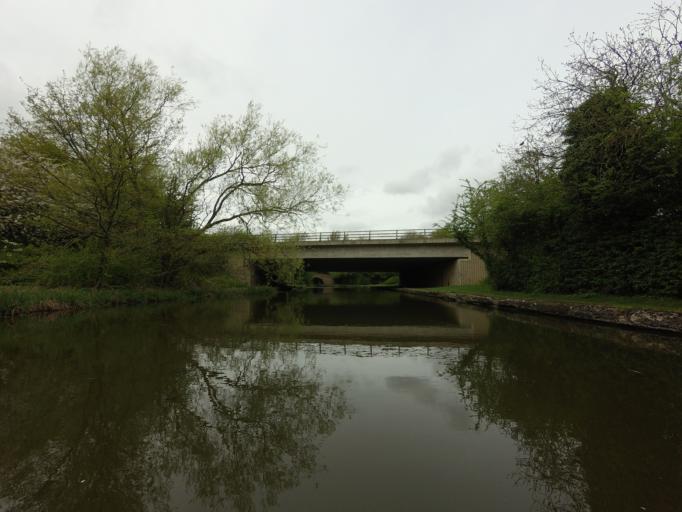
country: GB
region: England
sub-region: Milton Keynes
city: Simpson
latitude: 52.0253
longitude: -0.7245
